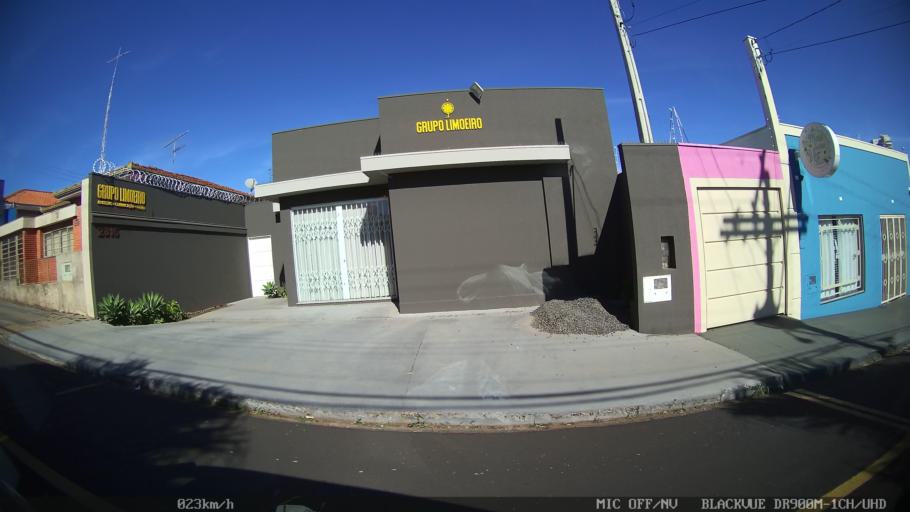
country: BR
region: Sao Paulo
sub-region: Franca
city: Franca
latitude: -20.5443
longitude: -47.3952
